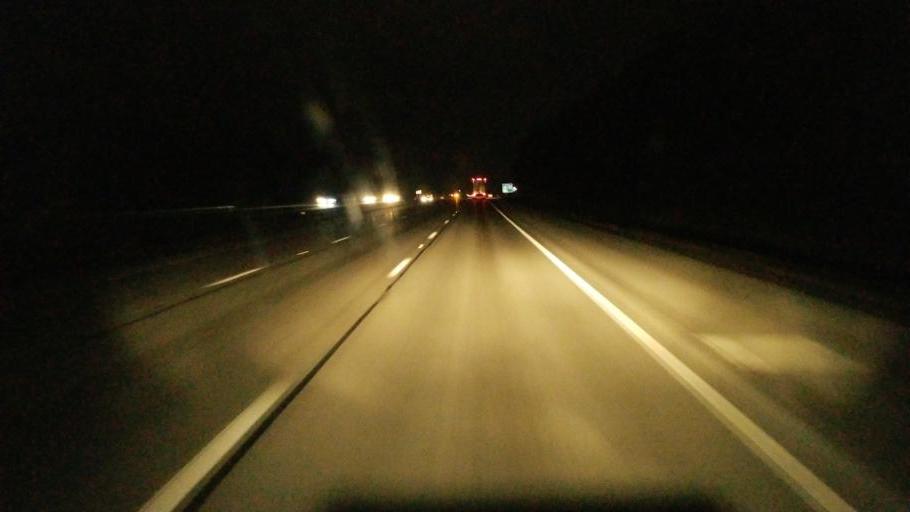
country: US
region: Ohio
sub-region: Clark County
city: Lisbon
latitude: 39.9125
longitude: -83.7032
